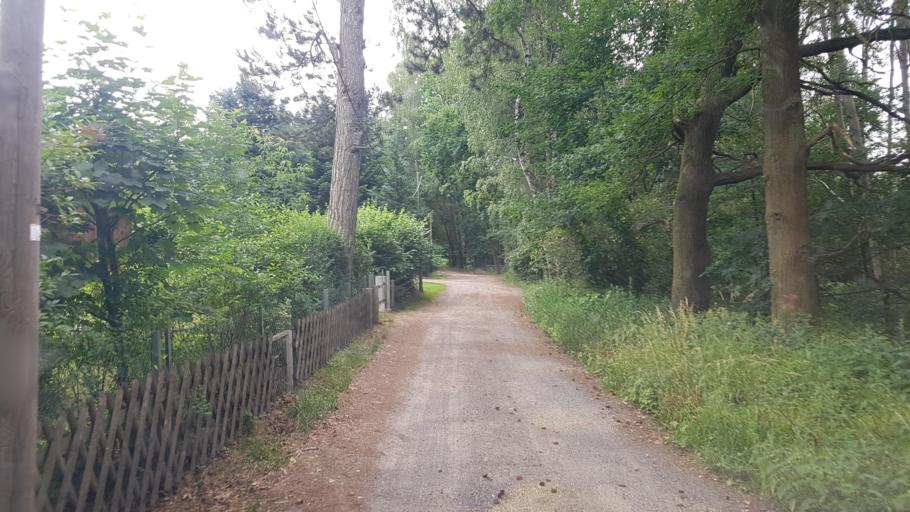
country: DE
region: Saxony-Anhalt
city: Kropstadt
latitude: 51.9425
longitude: 12.7117
